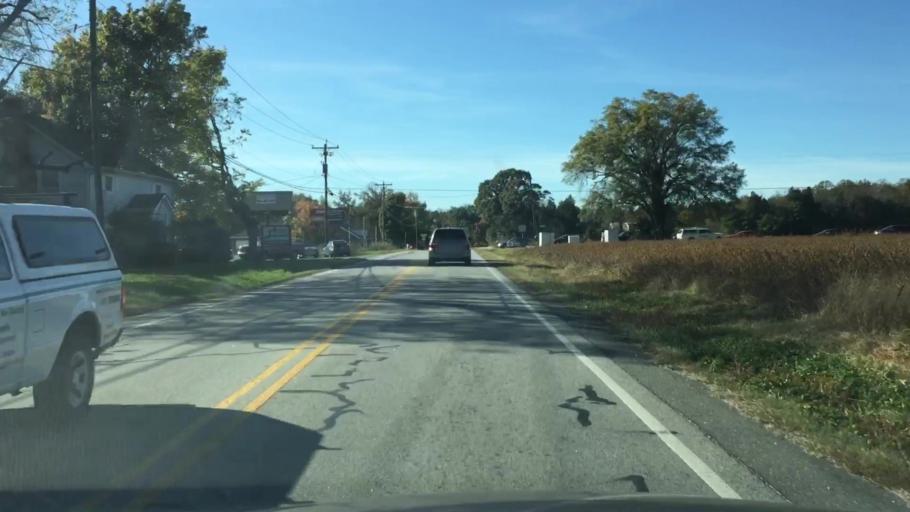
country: US
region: North Carolina
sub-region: Rowan County
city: China Grove
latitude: 35.6536
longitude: -80.5848
